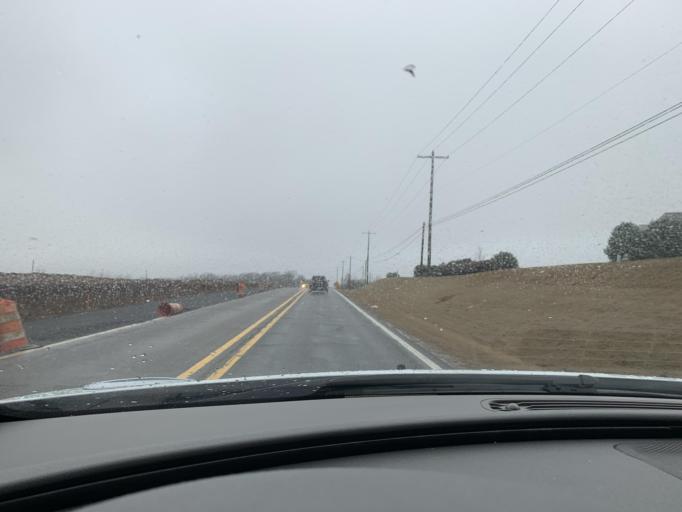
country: US
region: Mississippi
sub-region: De Soto County
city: Horn Lake
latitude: 34.9130
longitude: -90.0029
